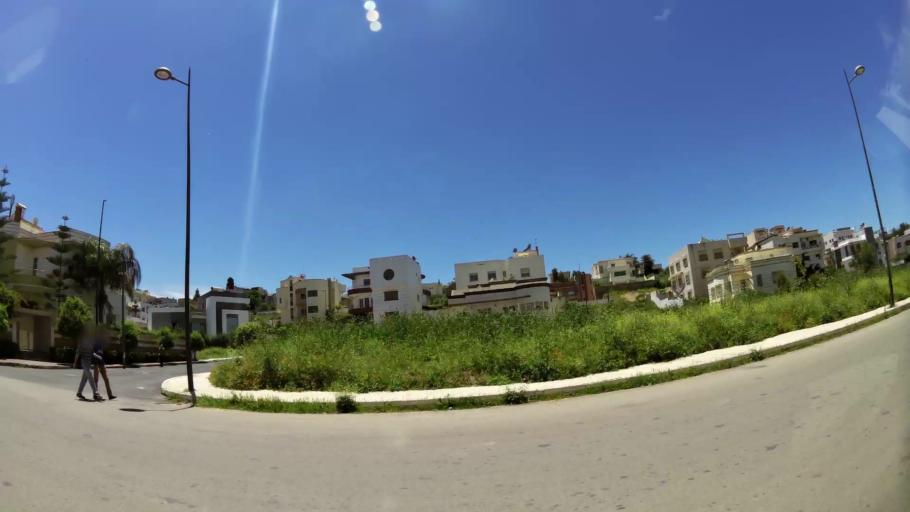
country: MA
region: Meknes-Tafilalet
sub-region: Meknes
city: Meknes
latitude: 33.9041
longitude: -5.5490
